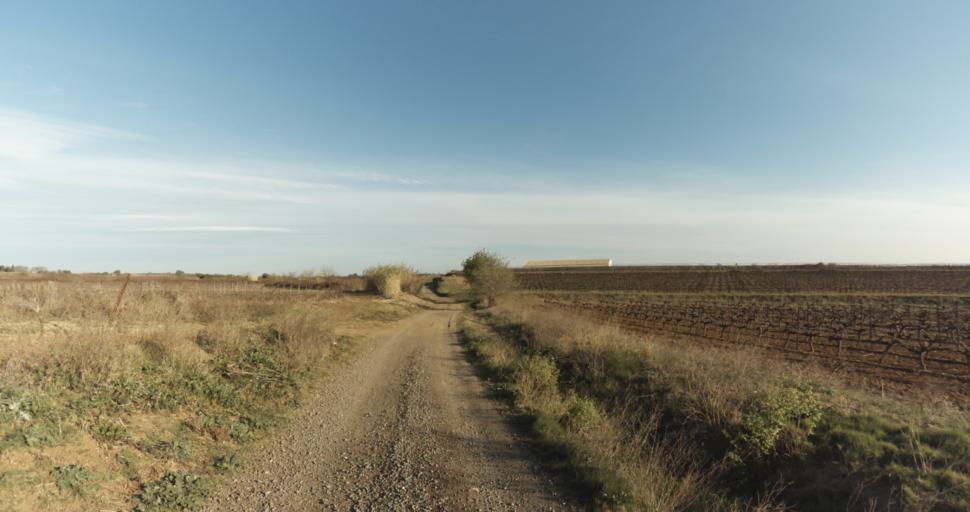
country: FR
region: Languedoc-Roussillon
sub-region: Departement de l'Herault
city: Pinet
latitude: 43.3877
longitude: 3.5198
